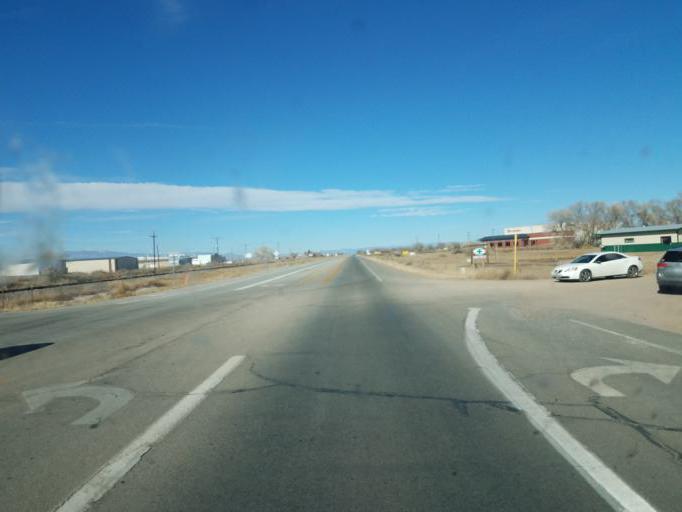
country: US
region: Colorado
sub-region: Alamosa County
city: Alamosa
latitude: 37.4903
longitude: -105.9300
